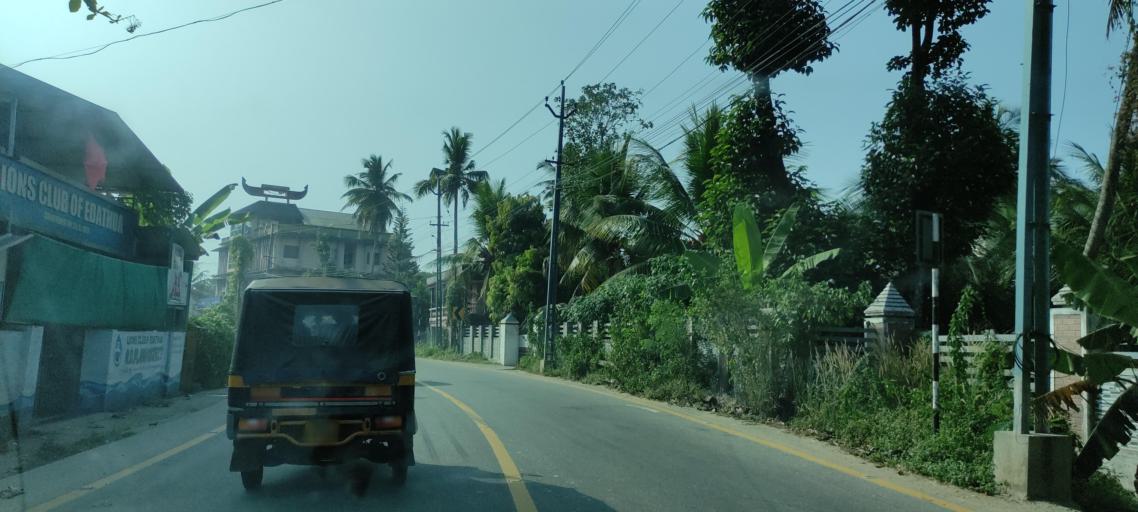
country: IN
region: Kerala
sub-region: Kottayam
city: Changanacheri
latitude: 9.3679
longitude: 76.4837
